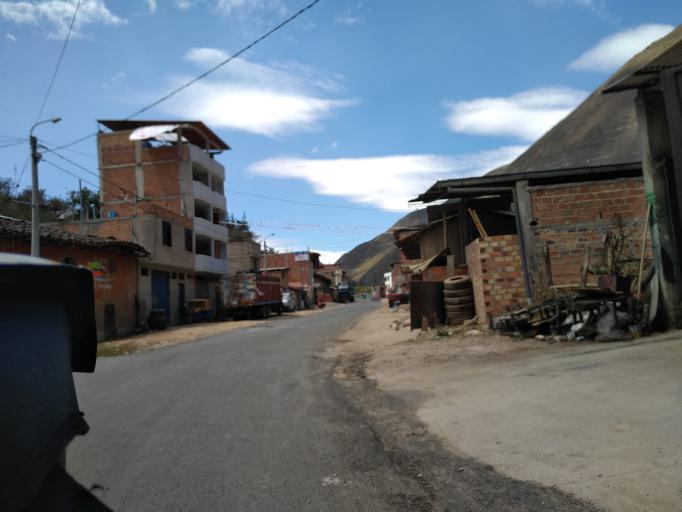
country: PE
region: Amazonas
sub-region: Provincia de Chachapoyas
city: Duraznopampa
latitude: -6.5655
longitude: -77.8294
